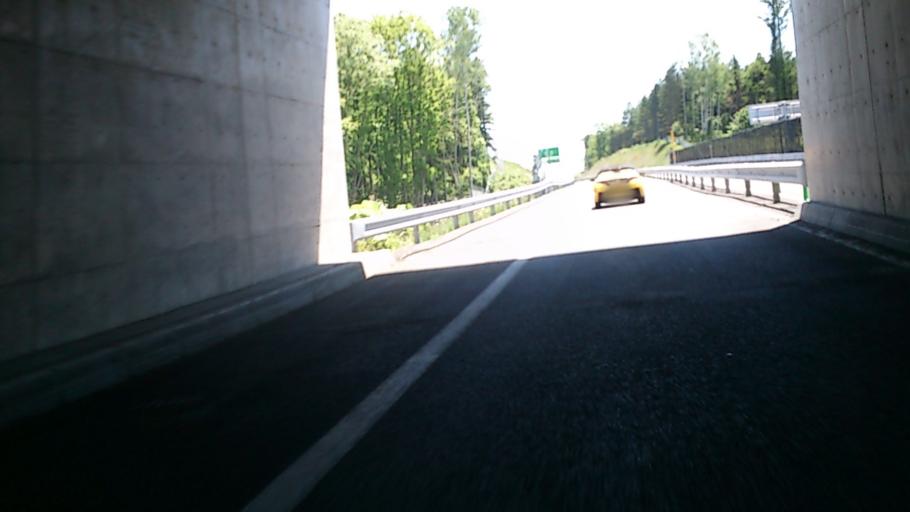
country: JP
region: Hokkaido
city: Nayoro
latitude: 44.4862
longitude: 142.3625
